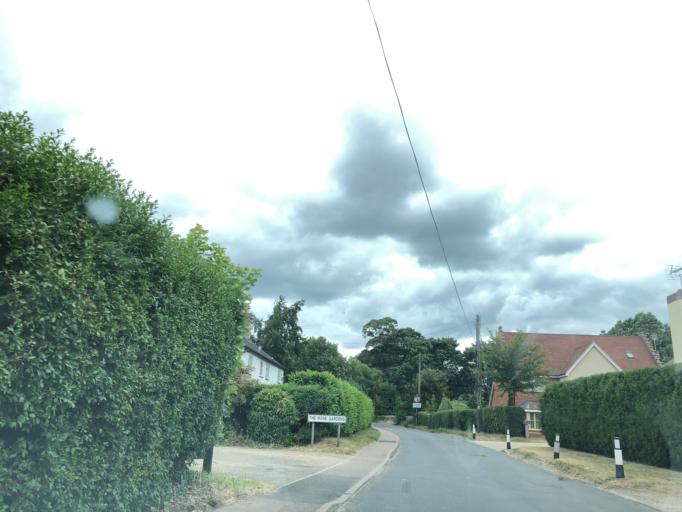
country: GB
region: England
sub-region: Suffolk
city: Thurston
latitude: 52.2489
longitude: 0.8140
